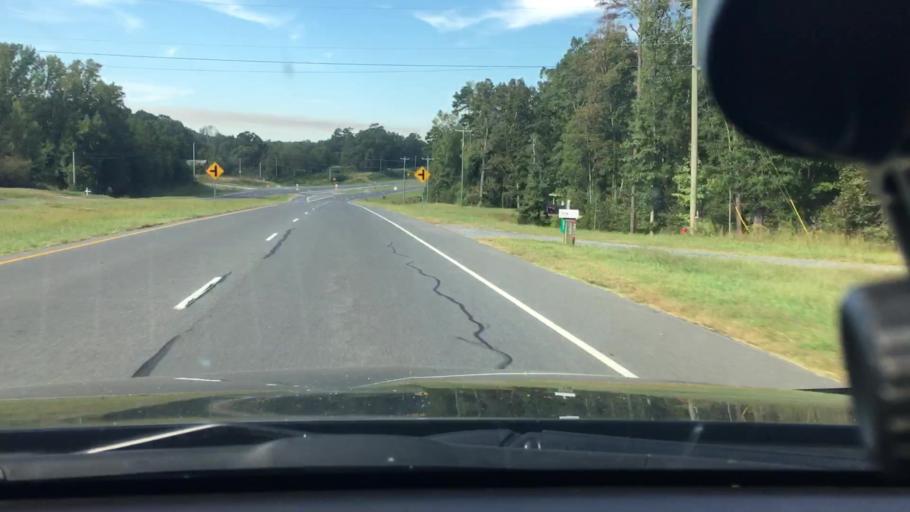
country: US
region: North Carolina
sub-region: Stanly County
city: Oakboro
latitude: 35.2705
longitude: -80.3331
